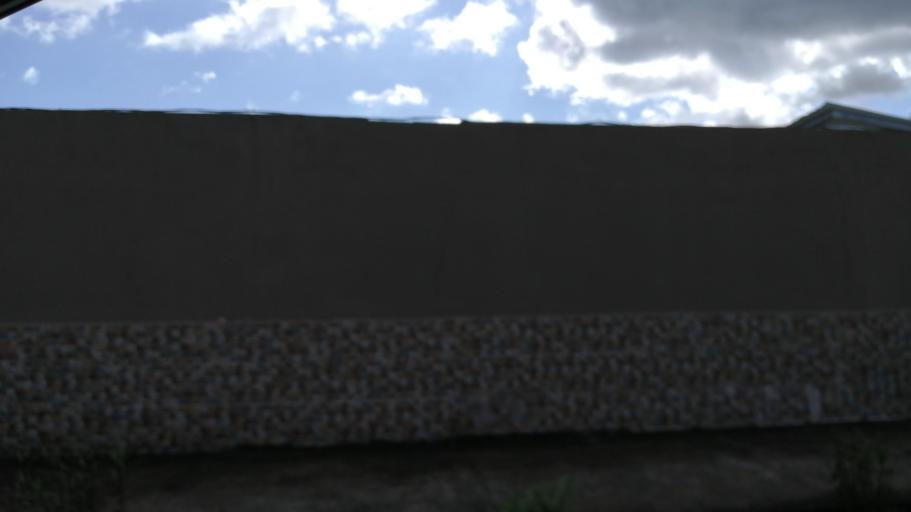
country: PA
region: Chiriqui
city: David
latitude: 8.4393
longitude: -82.4263
